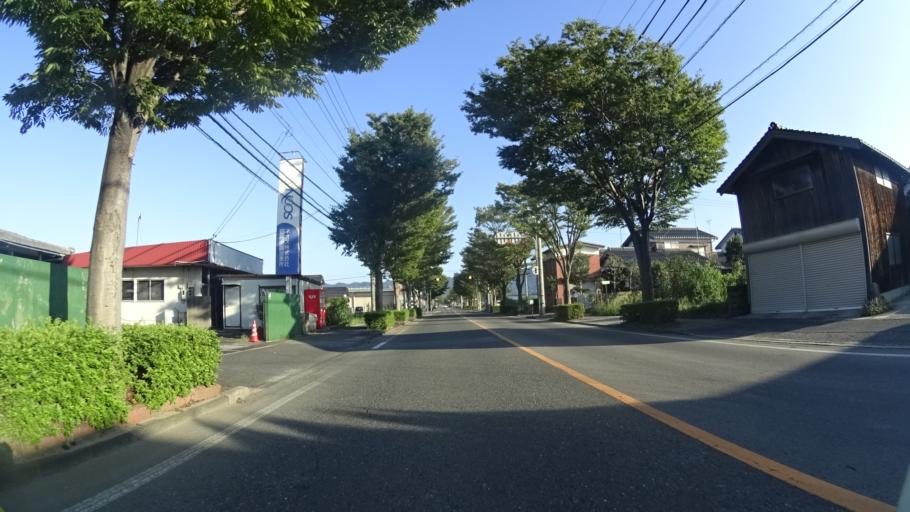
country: JP
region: Shimane
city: Sakaiminato
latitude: 35.5201
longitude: 133.2143
